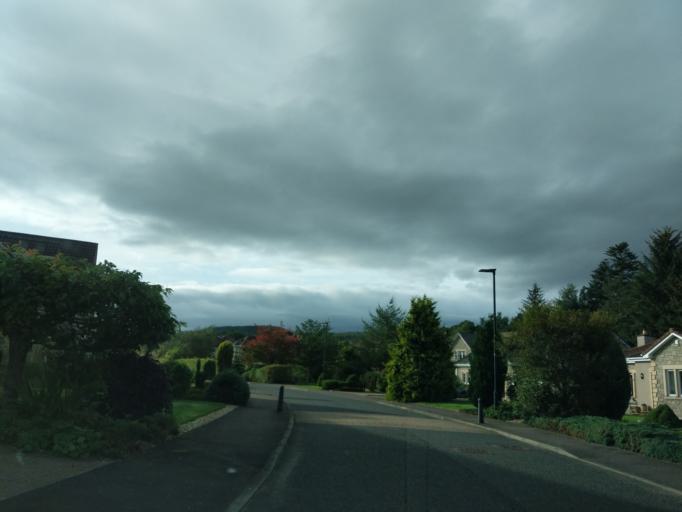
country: GB
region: Scotland
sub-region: The Scottish Borders
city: Innerleithen
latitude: 55.6393
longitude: -3.1041
